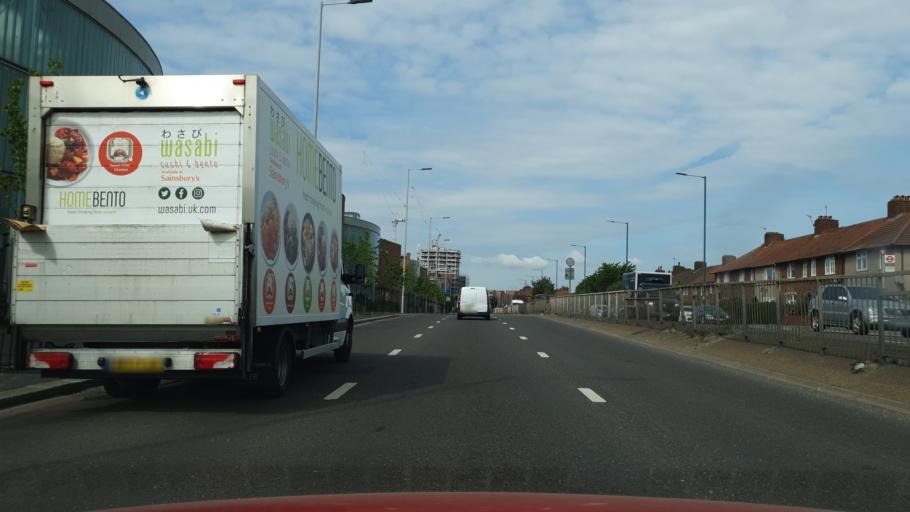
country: GB
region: England
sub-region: Greater London
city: Hammersmith
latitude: 51.5142
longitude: -0.2430
